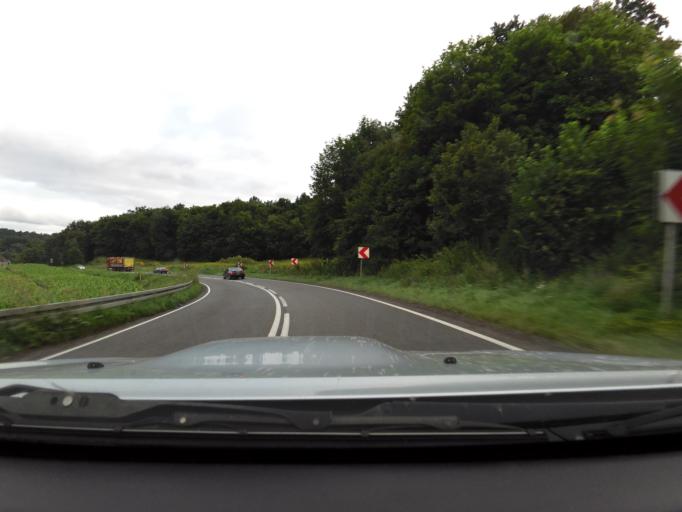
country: PL
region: Kujawsko-Pomorskie
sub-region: Powiat grudziadzki
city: Rogozno
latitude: 53.5192
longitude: 18.9404
